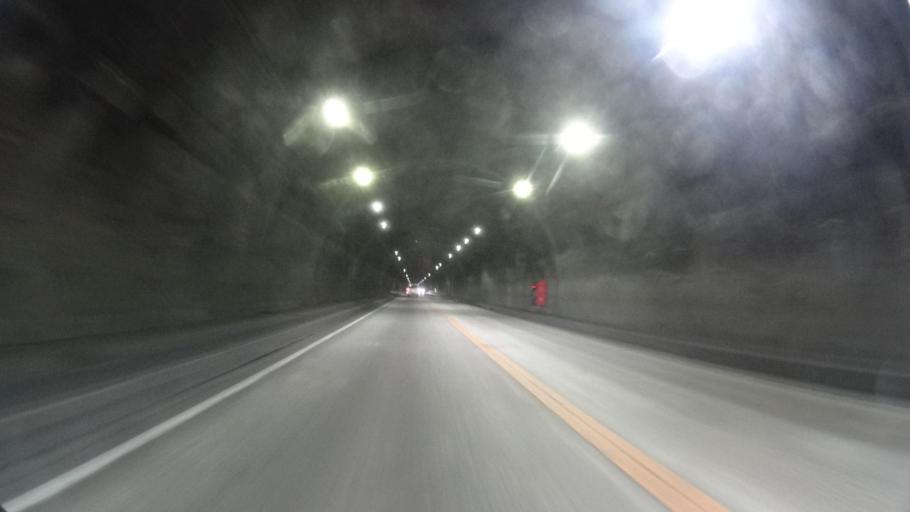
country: JP
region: Kyoto
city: Miyazu
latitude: 35.5473
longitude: 135.1824
